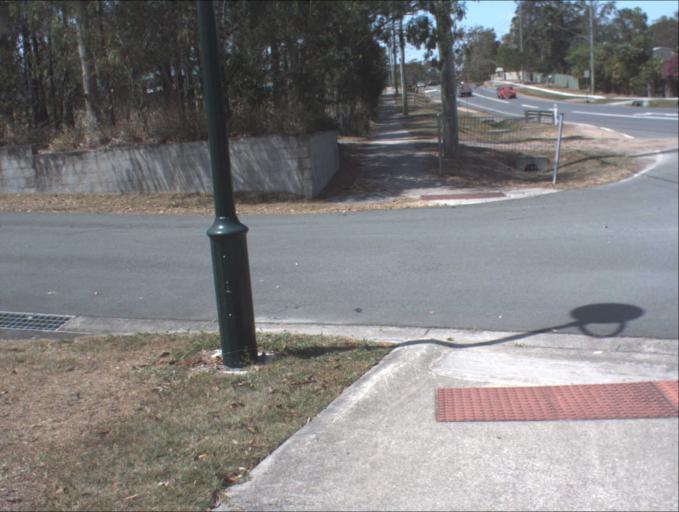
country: AU
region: Queensland
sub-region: Logan
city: Beenleigh
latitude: -27.6689
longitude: 153.2035
